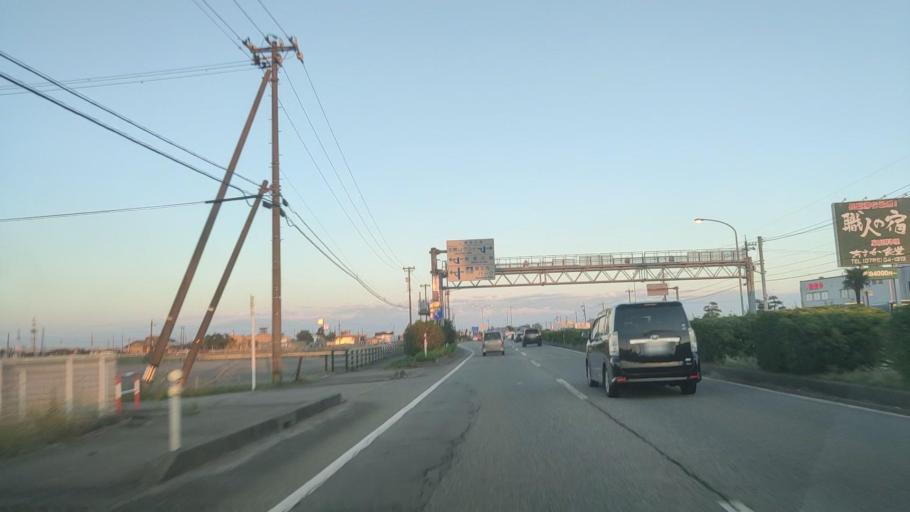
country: JP
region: Toyama
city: Nishishinminato
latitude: 36.7524
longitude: 137.0799
